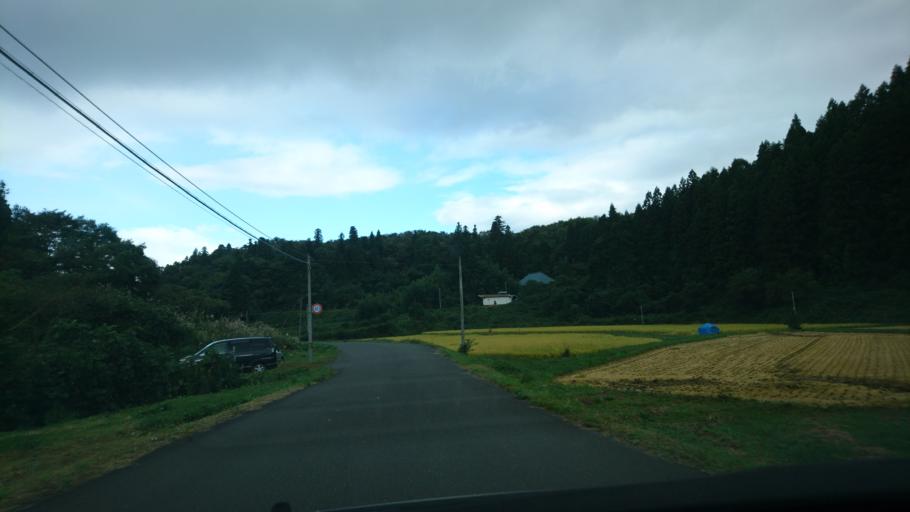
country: JP
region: Iwate
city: Ichinoseki
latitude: 38.9074
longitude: 141.0814
